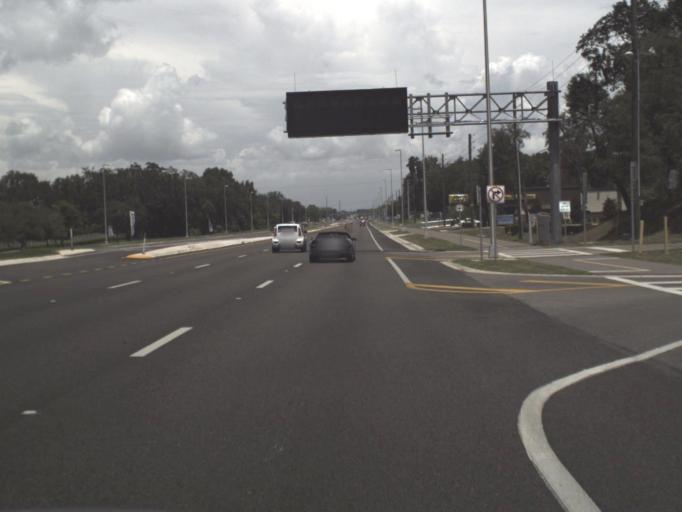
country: US
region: Florida
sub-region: Hillsborough County
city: Riverview
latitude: 27.8478
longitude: -82.3266
